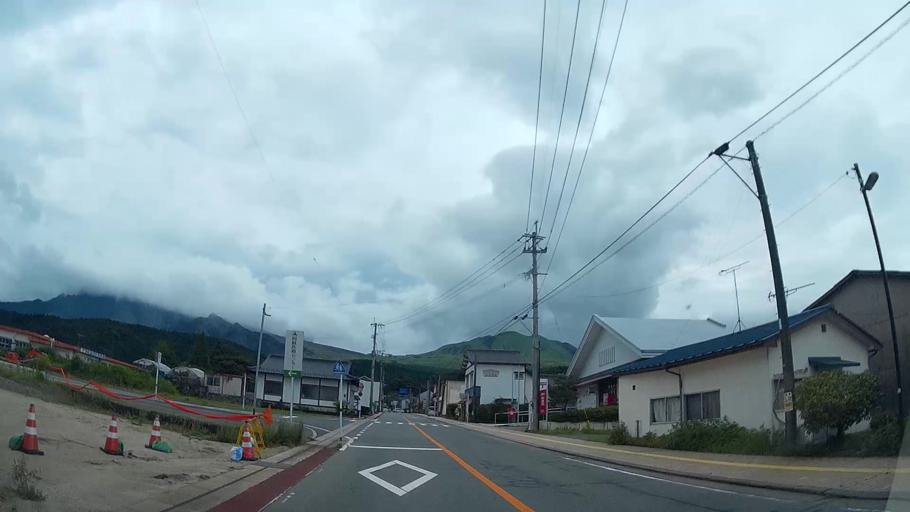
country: JP
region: Kumamoto
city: Aso
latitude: 32.9354
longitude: 131.0801
